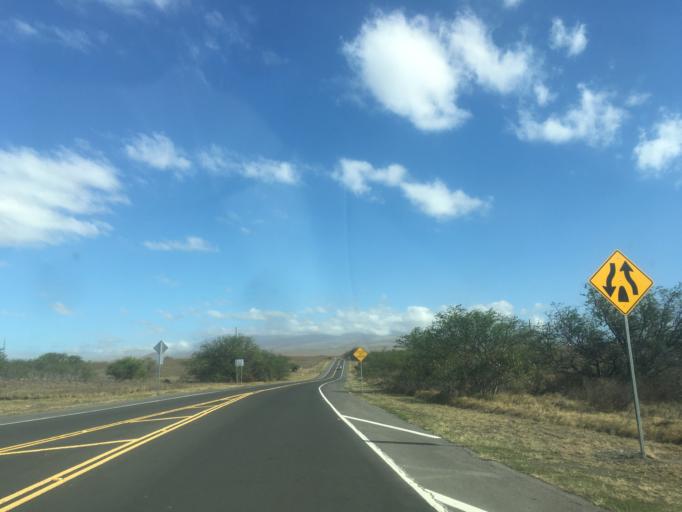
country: US
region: Hawaii
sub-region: Hawaii County
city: Waikoloa
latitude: 19.9258
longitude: -155.7849
